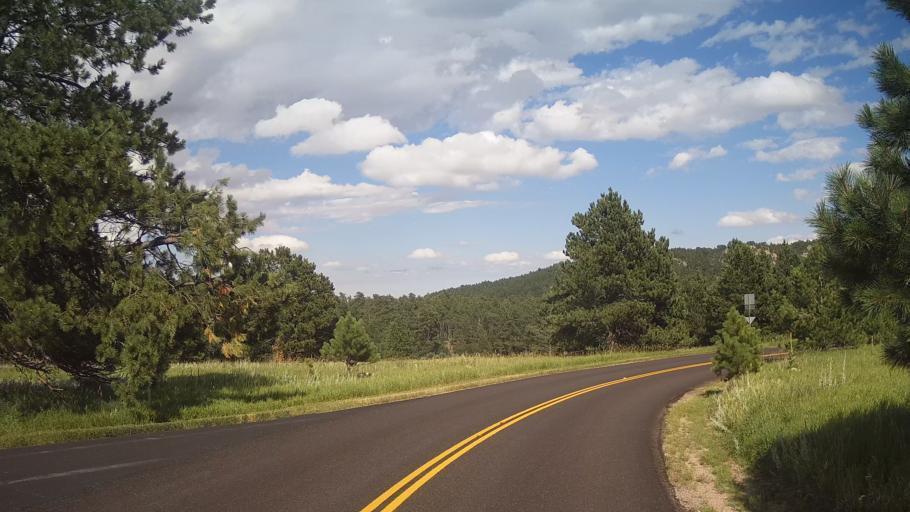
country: US
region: South Dakota
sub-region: Pennington County
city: Colonial Pine Hills
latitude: 43.8418
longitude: -103.3904
